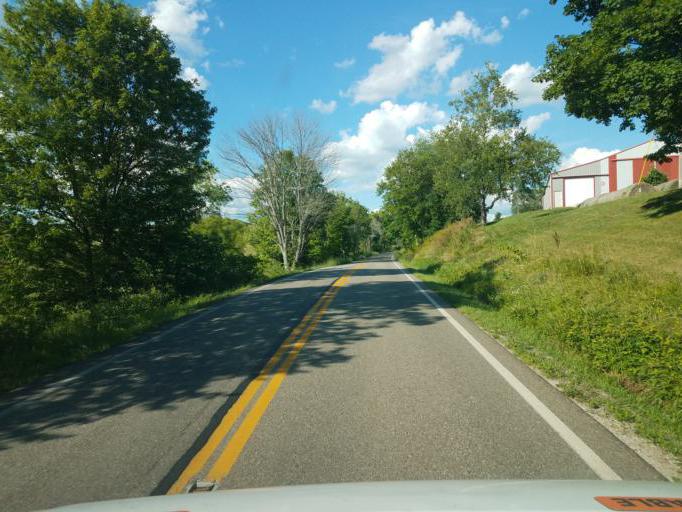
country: US
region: Ohio
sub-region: Gallia County
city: Gallipolis
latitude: 38.8025
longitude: -82.3241
